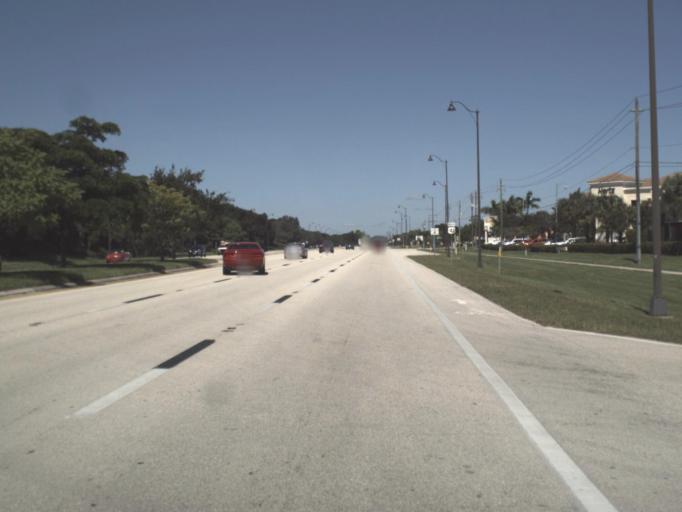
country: US
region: Florida
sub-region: Lee County
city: Bonita Springs
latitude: 26.3565
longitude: -81.8076
